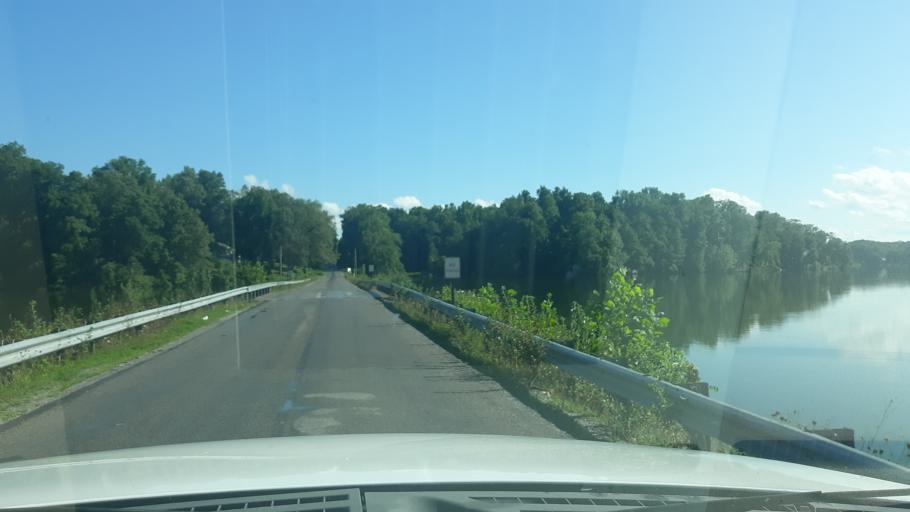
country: US
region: Illinois
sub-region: Saline County
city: Harrisburg
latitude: 37.8548
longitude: -88.5814
